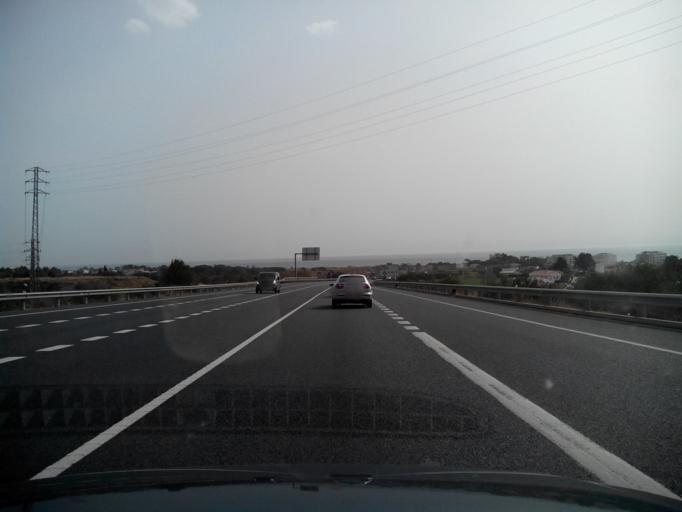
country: ES
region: Catalonia
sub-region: Provincia de Tarragona
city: Creixell
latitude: 41.1596
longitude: 1.4196
